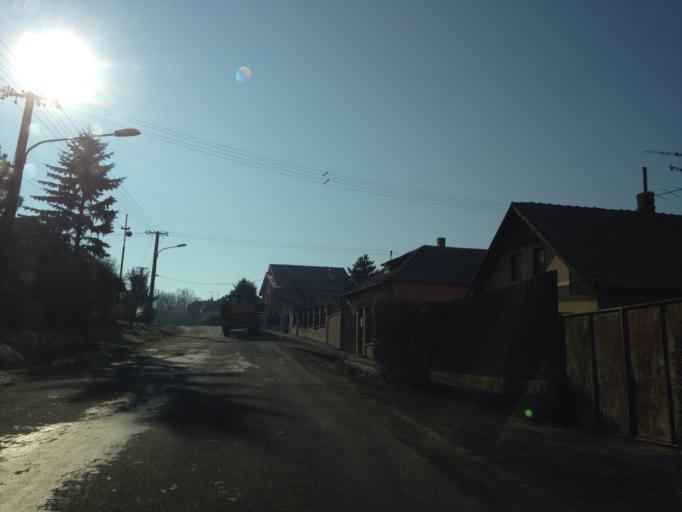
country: SK
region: Nitriansky
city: Svodin
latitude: 47.9499
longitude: 18.4130
